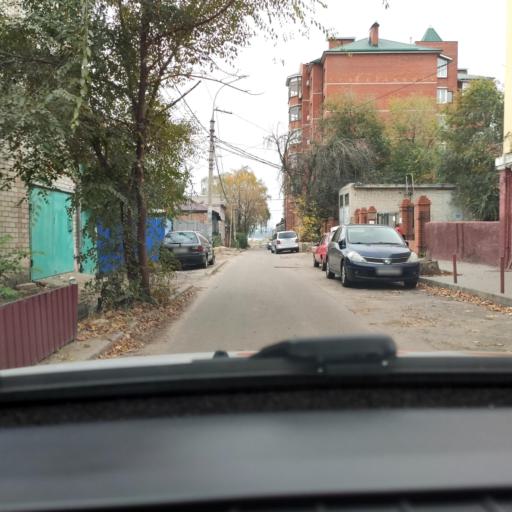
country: RU
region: Voronezj
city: Voronezh
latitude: 51.6729
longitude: 39.2210
